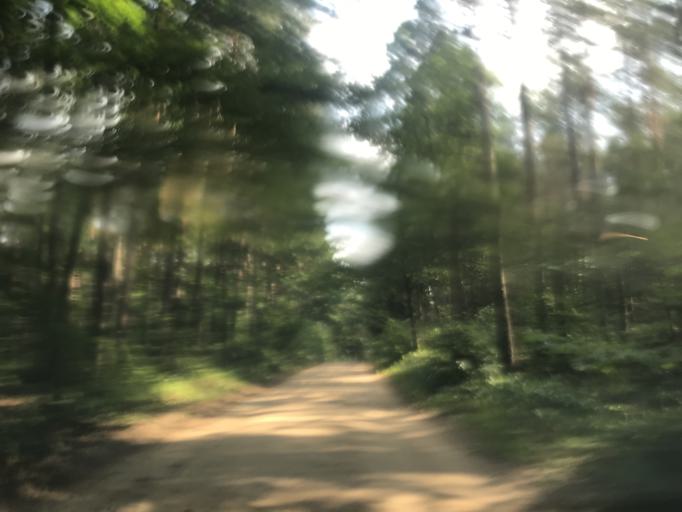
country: PL
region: Kujawsko-Pomorskie
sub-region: Powiat brodnicki
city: Brodnica
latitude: 53.3574
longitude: 19.4524
